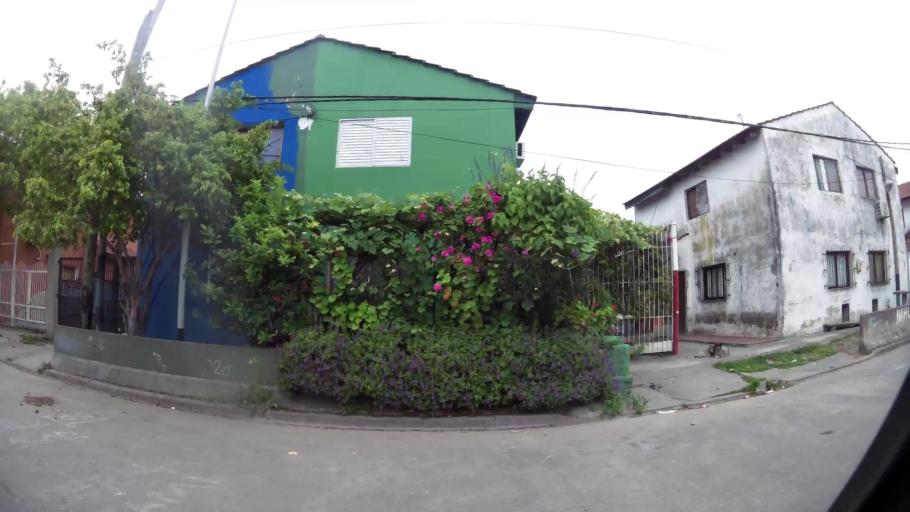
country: AR
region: Buenos Aires
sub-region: Partido de Avellaneda
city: Avellaneda
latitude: -34.6428
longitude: -58.3471
